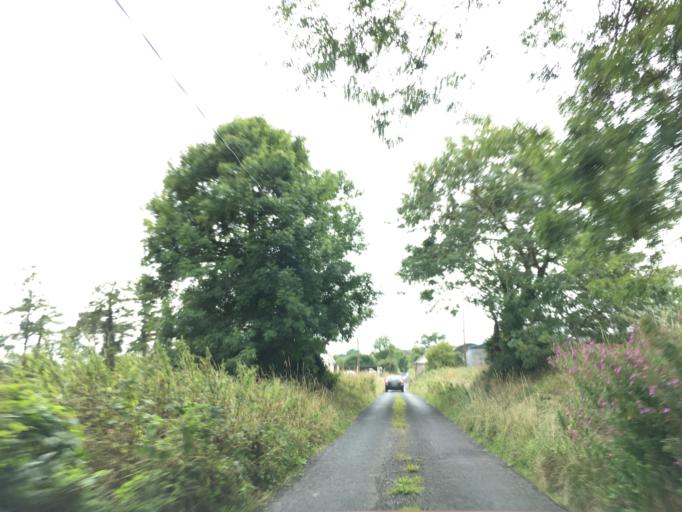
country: IE
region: Munster
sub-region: An Clar
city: Ennis
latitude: 52.7290
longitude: -9.0659
